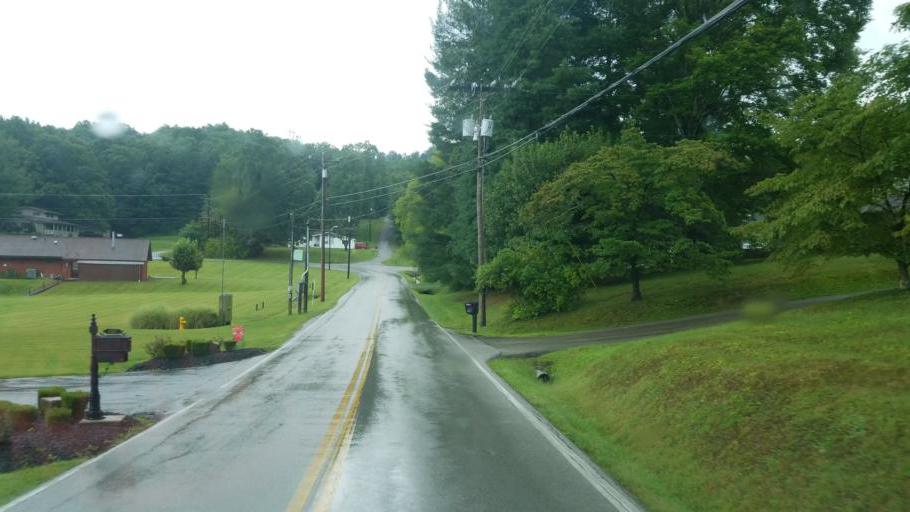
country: US
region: Kentucky
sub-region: Rowan County
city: Morehead
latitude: 38.1817
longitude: -83.4842
